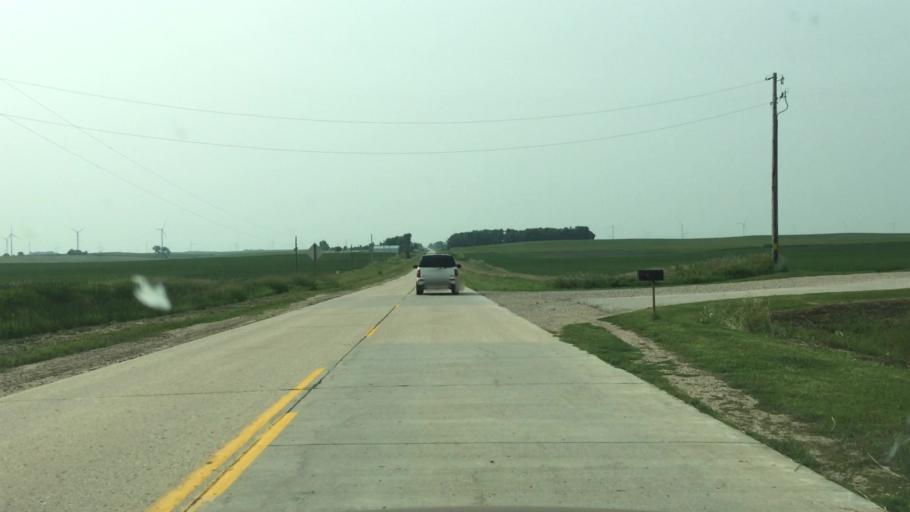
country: US
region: Iowa
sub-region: Dickinson County
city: Lake Park
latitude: 43.4285
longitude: -95.2891
